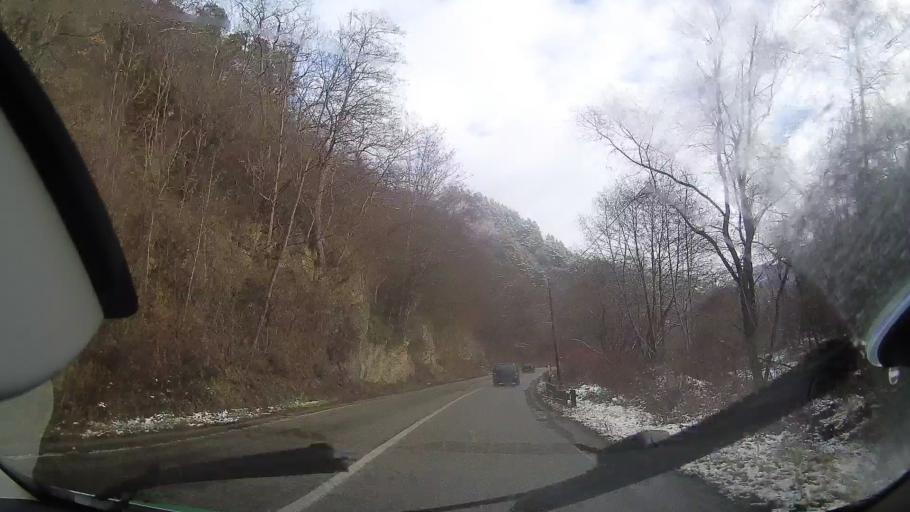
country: RO
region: Alba
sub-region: Oras Baia de Aries
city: Baia de Aries
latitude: 46.4017
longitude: 23.3024
